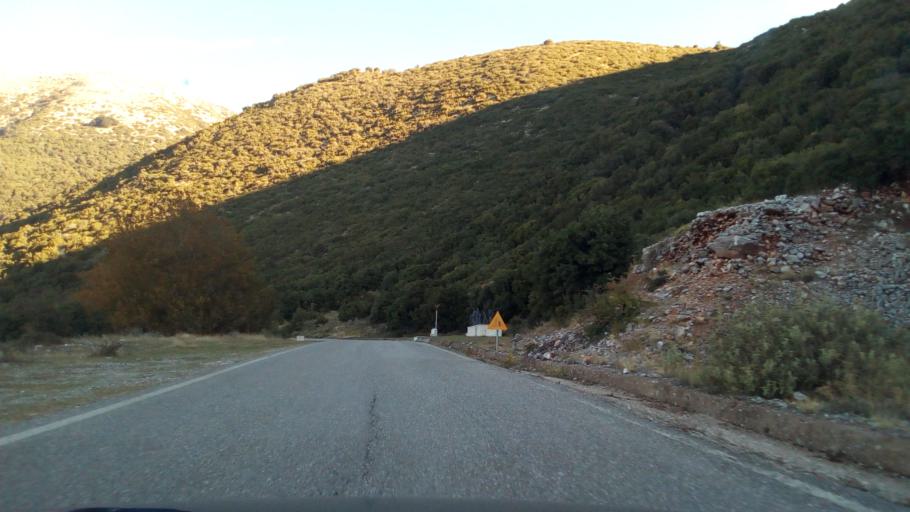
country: GR
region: West Greece
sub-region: Nomos Aitolias kai Akarnanias
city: Nafpaktos
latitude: 38.4904
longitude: 21.8579
